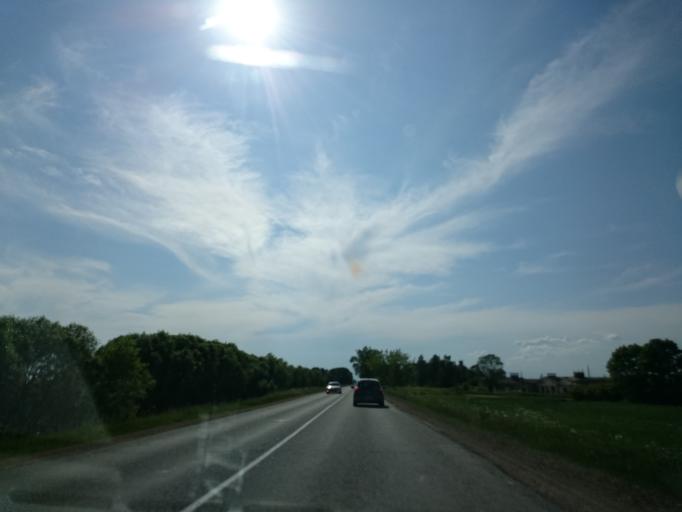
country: LV
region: Jelgava
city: Jelgava
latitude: 56.6235
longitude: 23.5336
